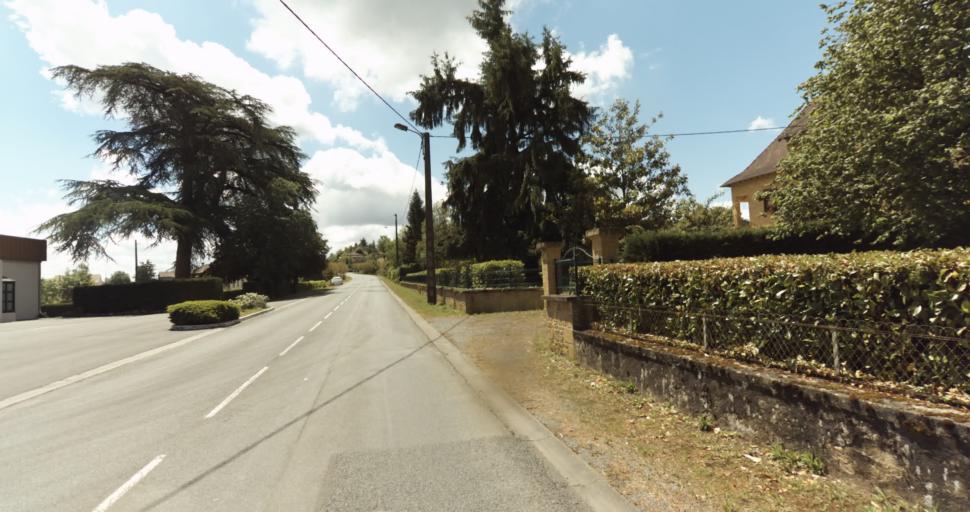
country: FR
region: Aquitaine
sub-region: Departement de la Dordogne
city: Beaumont-du-Perigord
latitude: 44.7748
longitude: 0.7648
